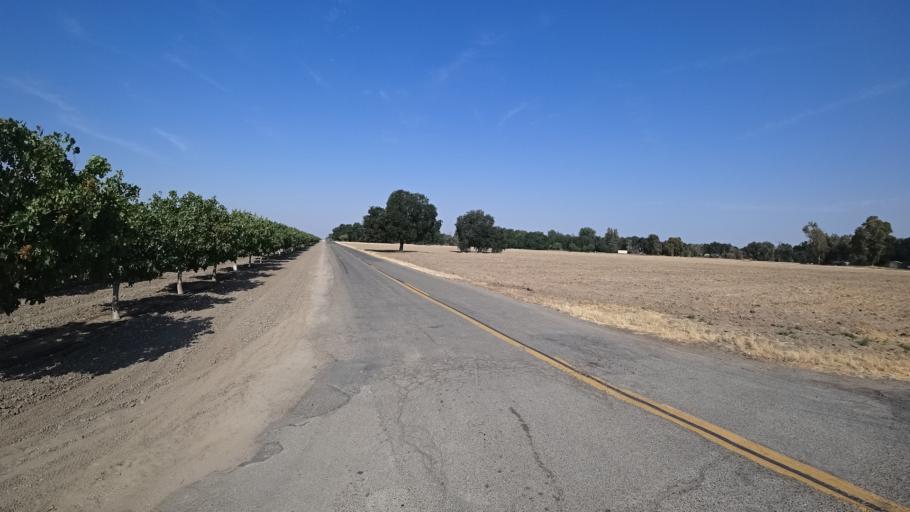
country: US
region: California
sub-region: Kings County
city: Lemoore
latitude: 36.3286
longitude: -119.8515
